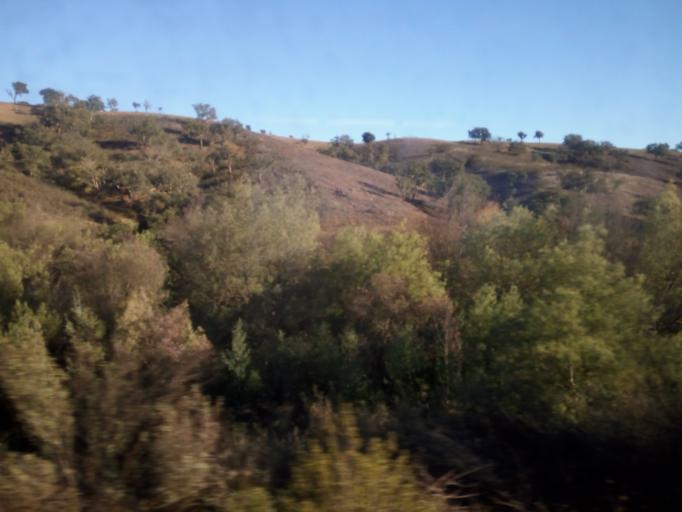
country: PT
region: Beja
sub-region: Odemira
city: Odemira
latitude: 37.5847
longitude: -8.4928
